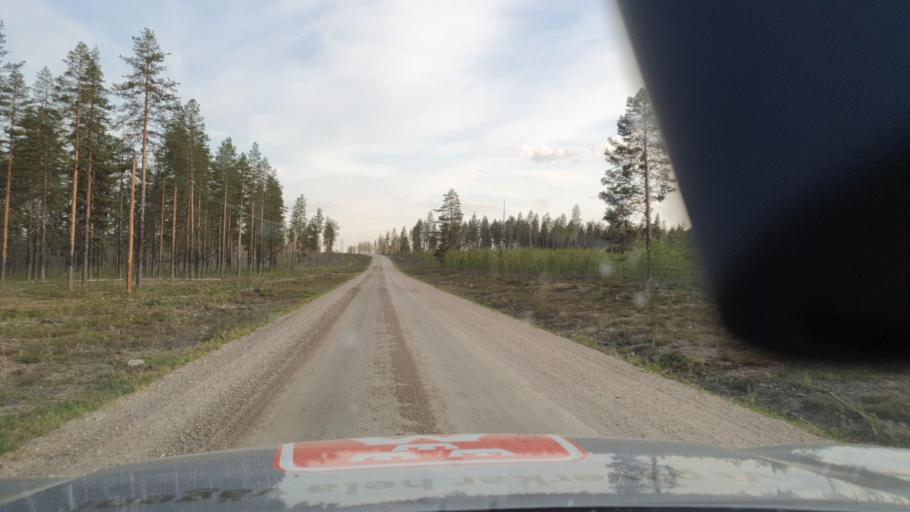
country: SE
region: Norrbotten
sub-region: Bodens Kommun
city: Boden
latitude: 66.3306
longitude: 21.4079
